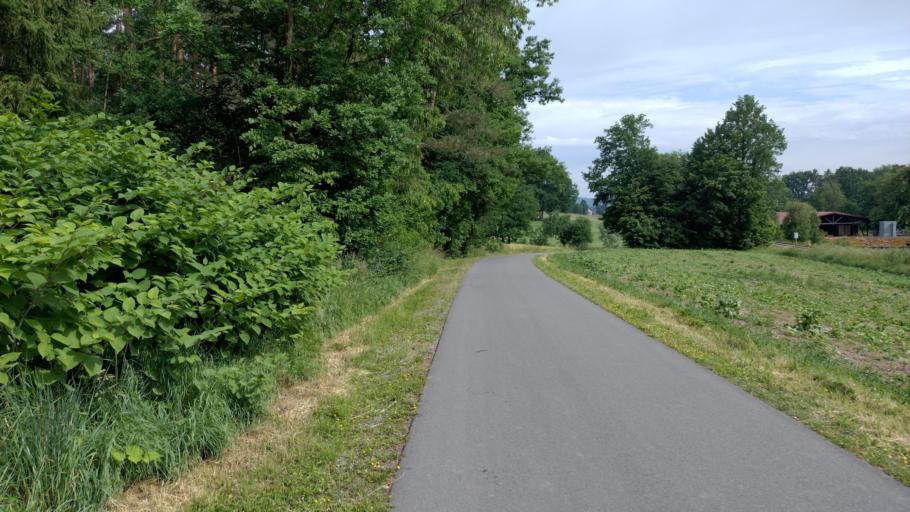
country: DE
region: Bavaria
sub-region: Upper Franconia
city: Harsdorf
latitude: 50.0177
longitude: 11.5774
